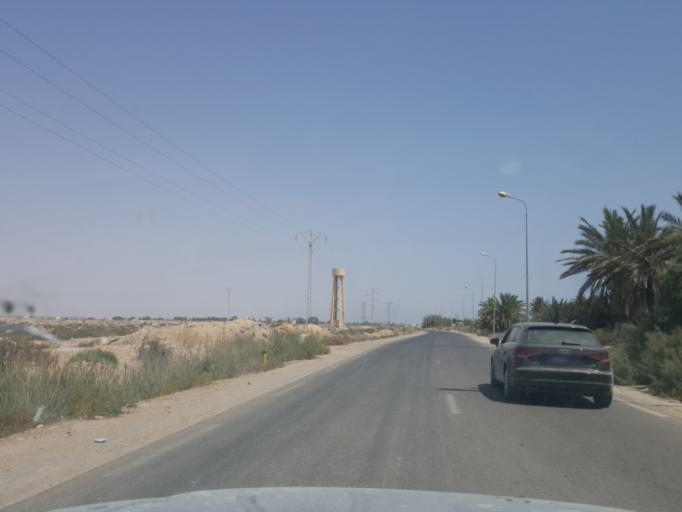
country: TN
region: Qabis
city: Gabes
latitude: 33.9702
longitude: 10.0003
